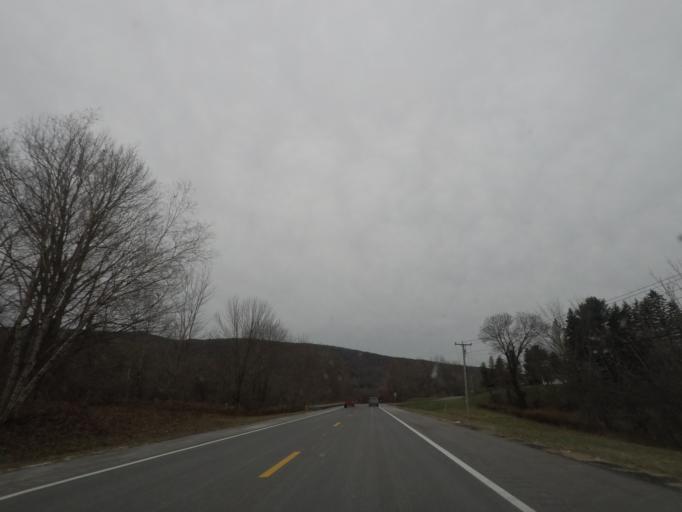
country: US
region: Massachusetts
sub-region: Berkshire County
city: Lanesborough
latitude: 42.5475
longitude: -73.3124
